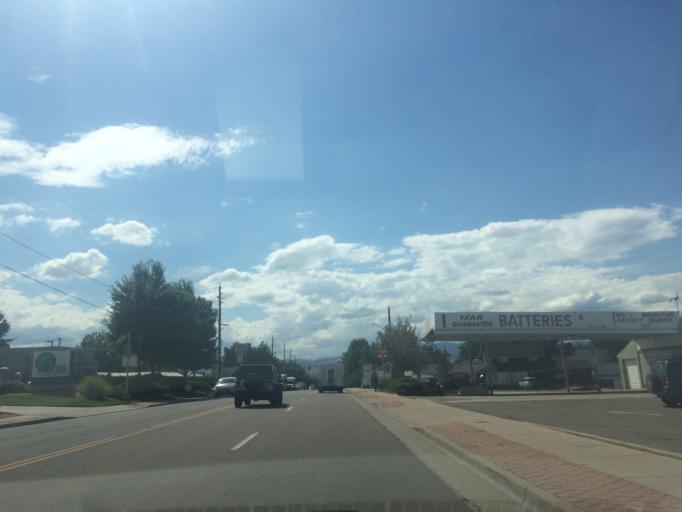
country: US
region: Colorado
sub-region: Jefferson County
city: Wheat Ridge
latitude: 39.7767
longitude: -105.0852
